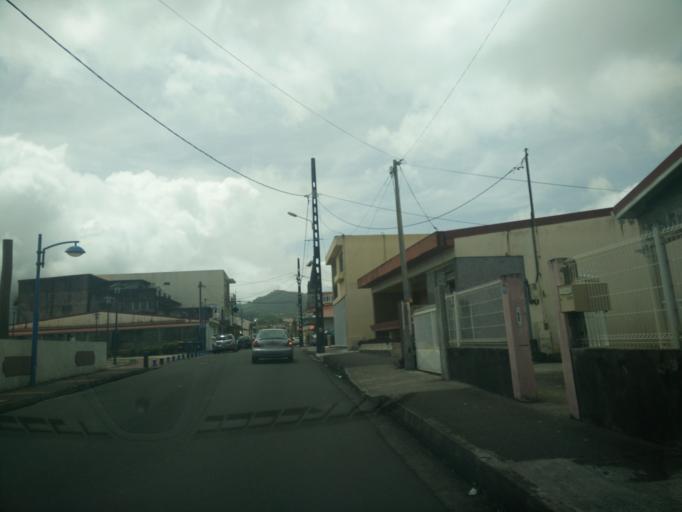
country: MQ
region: Martinique
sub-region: Martinique
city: Le Morne-Rouge
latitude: 14.7734
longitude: -61.1352
